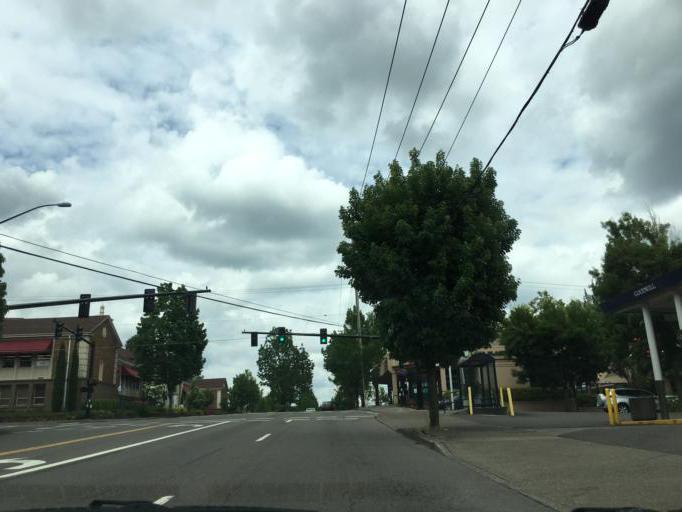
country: US
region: Oregon
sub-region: Clackamas County
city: Lake Oswego
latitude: 45.4126
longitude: -122.6643
